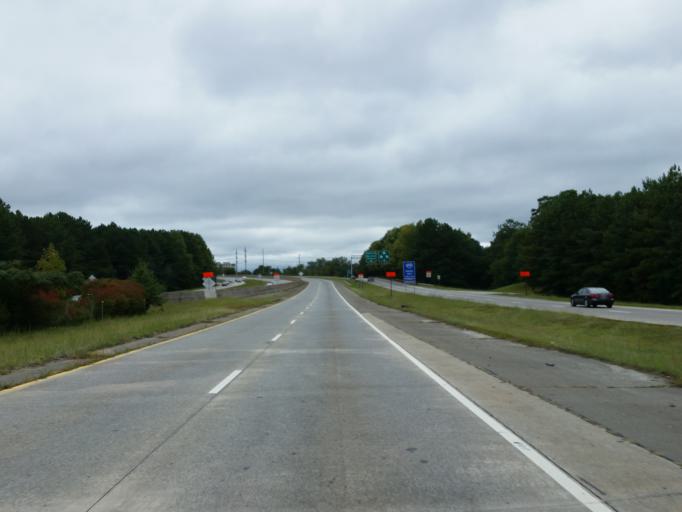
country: US
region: Georgia
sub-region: Cobb County
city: Marietta
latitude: 33.9814
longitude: -84.5460
